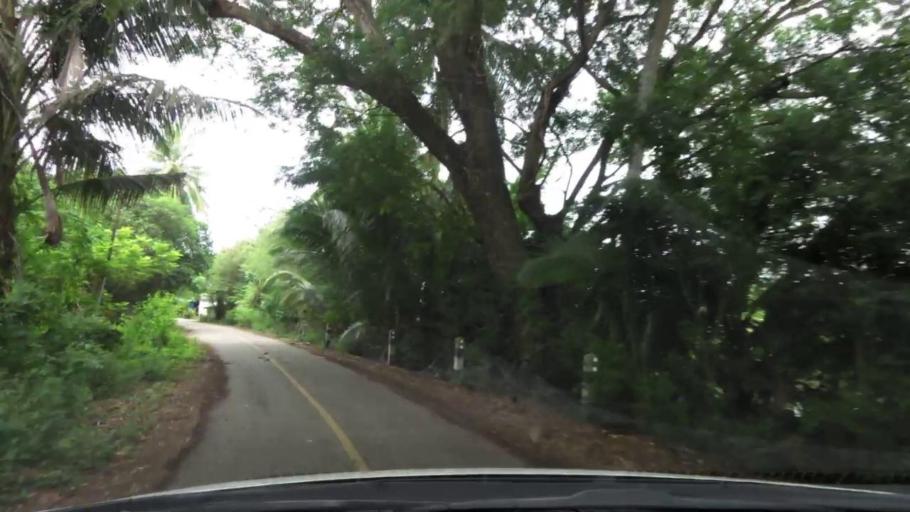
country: TH
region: Samut Sakhon
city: Ban Phaeo
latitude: 13.6077
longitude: 100.0267
